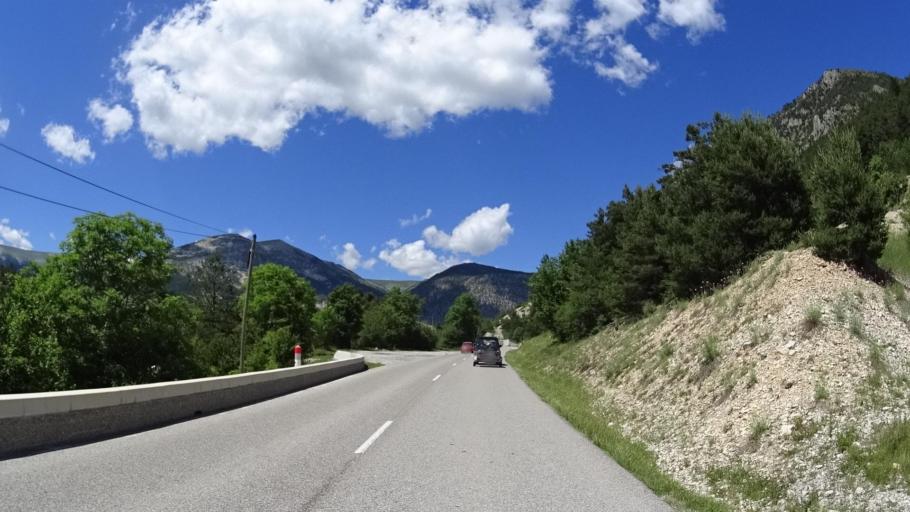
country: FR
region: Provence-Alpes-Cote d'Azur
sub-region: Departement des Alpes-de-Haute-Provence
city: Annot
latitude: 44.0789
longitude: 6.5684
